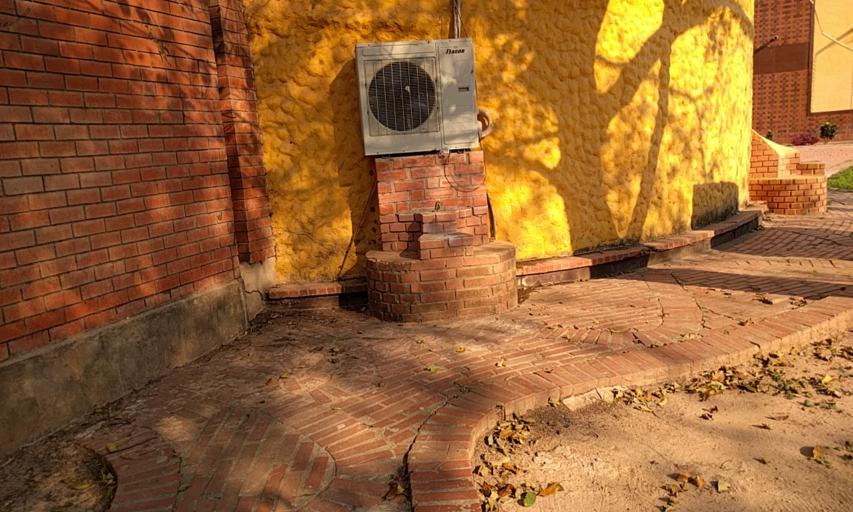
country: BO
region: Santa Cruz
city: Warnes
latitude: -17.4480
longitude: -63.1853
